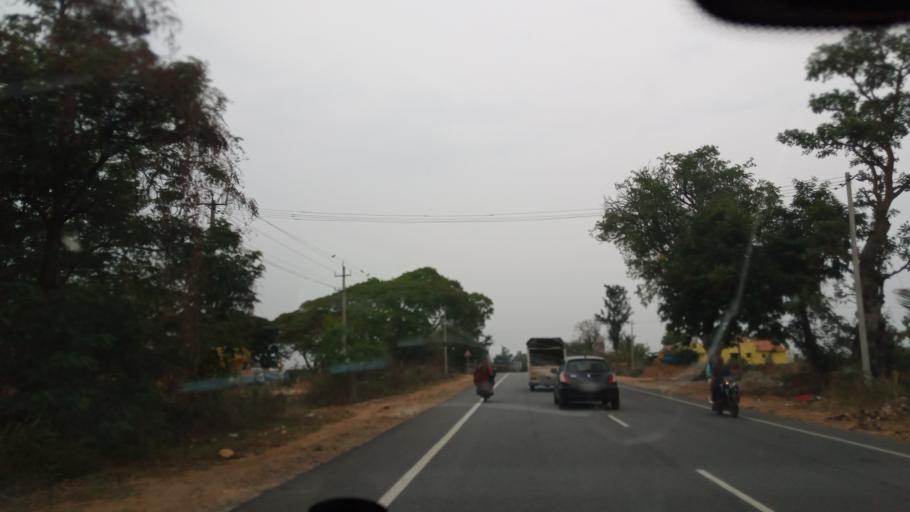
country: IN
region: Karnataka
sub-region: Mandya
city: Belluru
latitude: 12.9357
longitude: 76.7502
